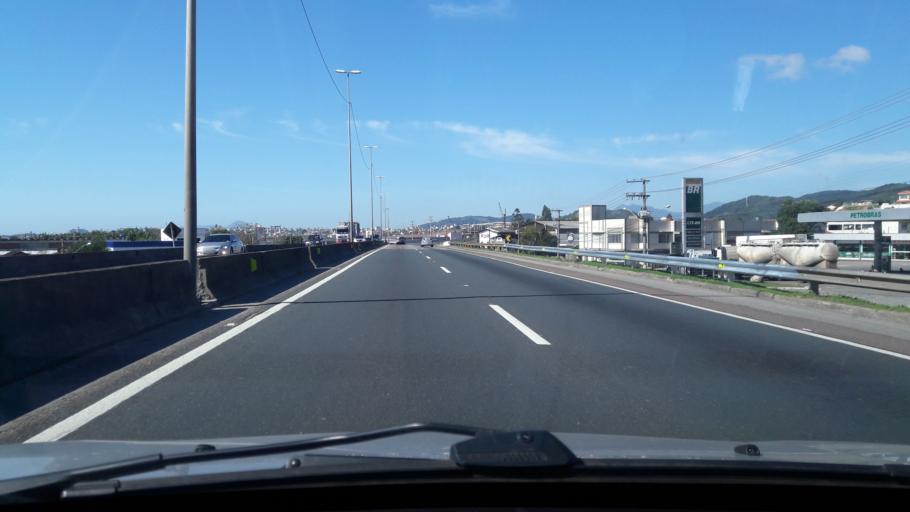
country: BR
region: Santa Catarina
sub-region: Biguacu
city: Biguacu
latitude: -27.5203
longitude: -48.6376
